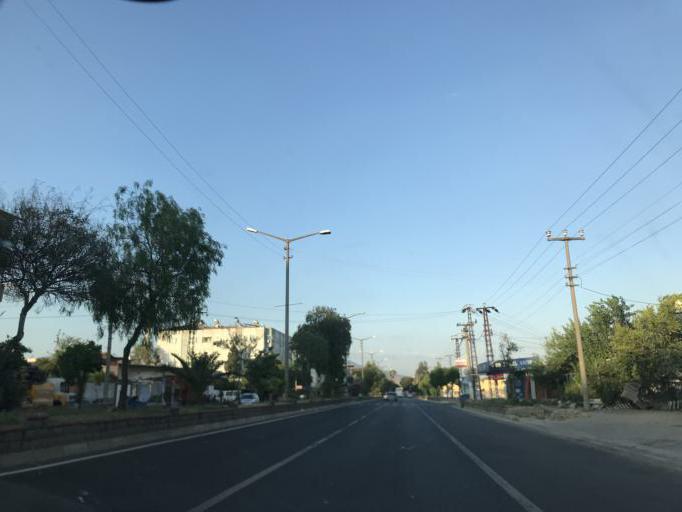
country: TR
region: Aydin
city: Nazilli
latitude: 37.9074
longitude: 28.3095
